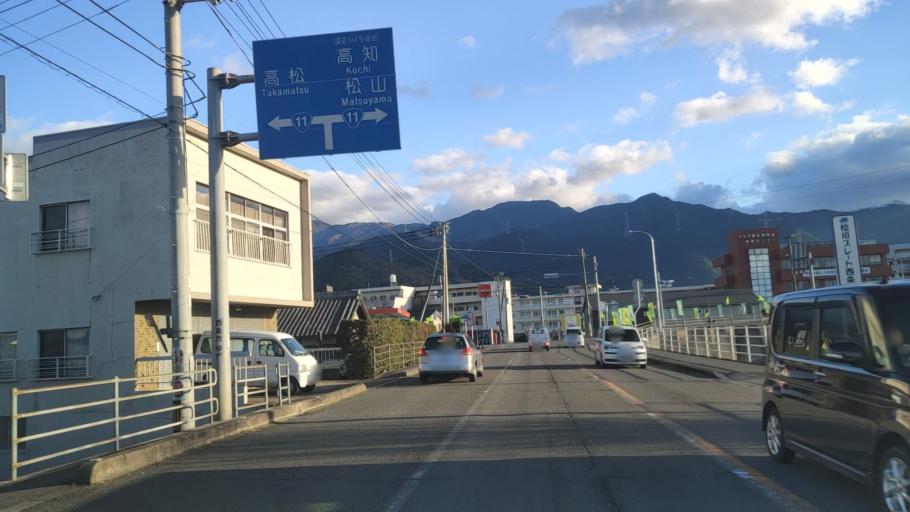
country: JP
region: Ehime
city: Saijo
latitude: 33.9064
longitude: 133.1859
